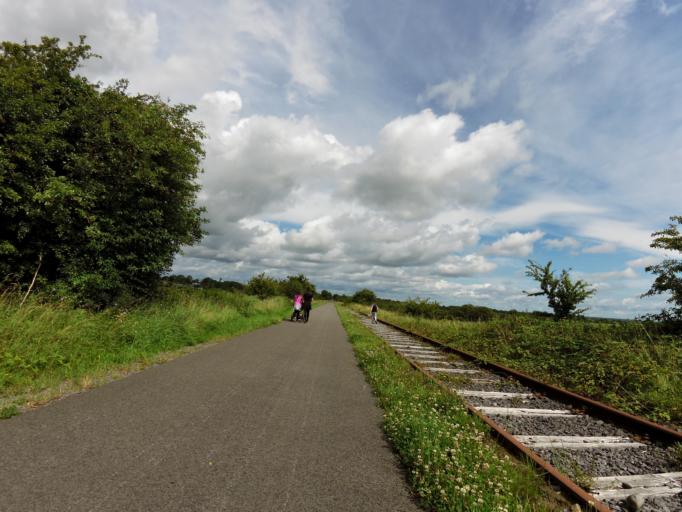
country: IE
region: Leinster
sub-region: An Iarmhi
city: Kilbeggan
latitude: 53.4690
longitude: -7.4953
